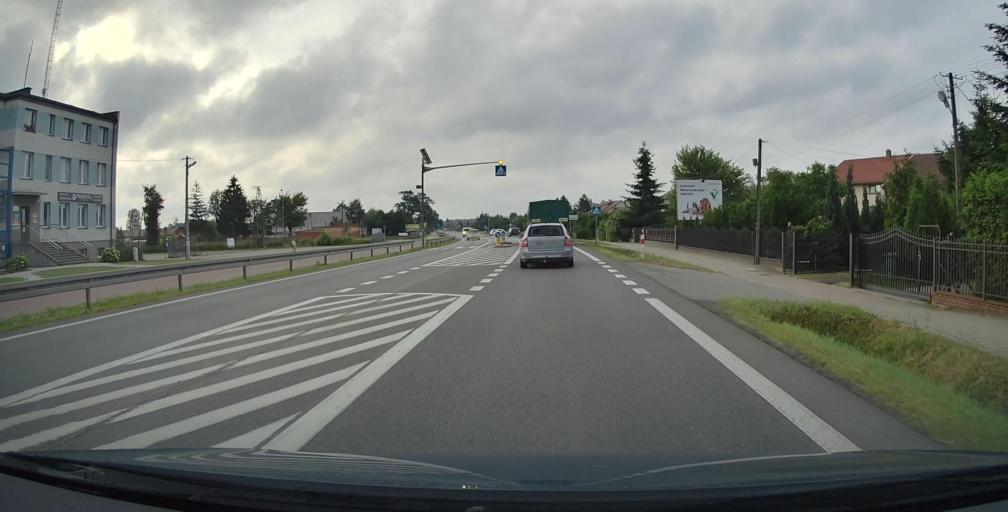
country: PL
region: Masovian Voivodeship
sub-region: Powiat siedlecki
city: Zbuczyn
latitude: 52.0880
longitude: 22.4425
